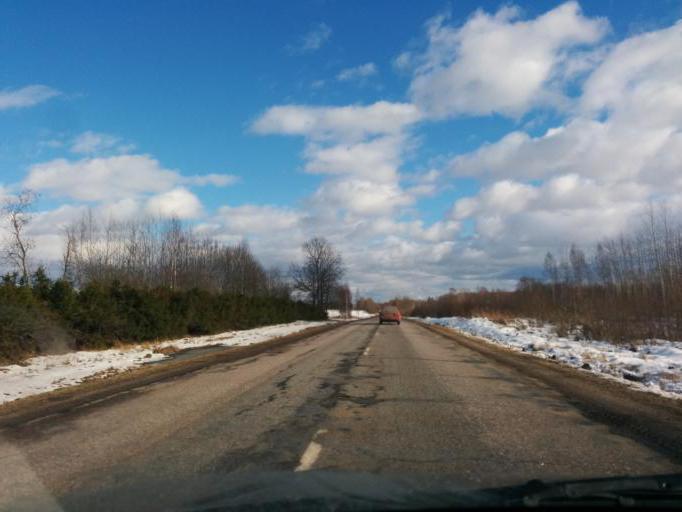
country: LV
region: Balvu Rajons
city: Balvi
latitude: 57.1623
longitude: 27.1718
